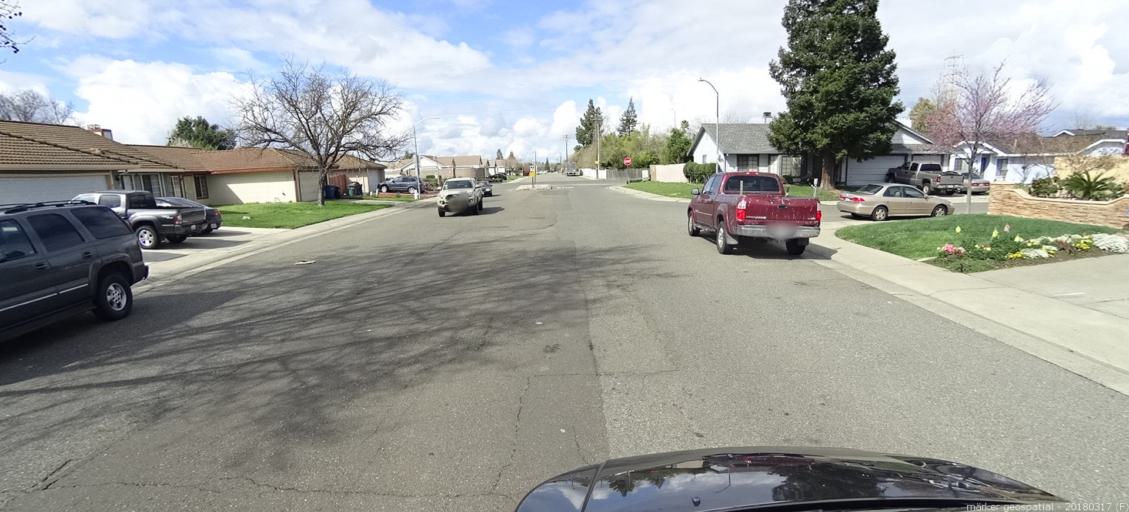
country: US
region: California
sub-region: Sacramento County
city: Florin
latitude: 38.4689
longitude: -121.4079
